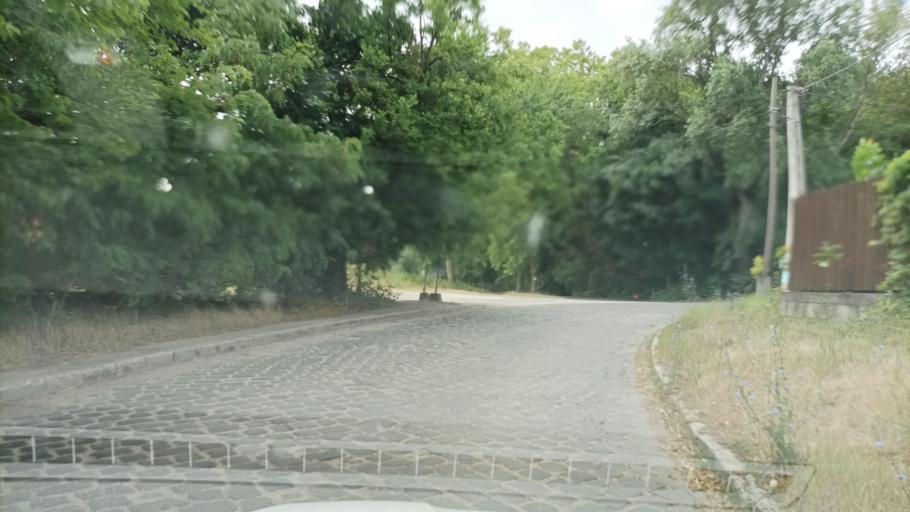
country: HU
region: Pest
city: Vac
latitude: 47.7738
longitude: 19.1192
